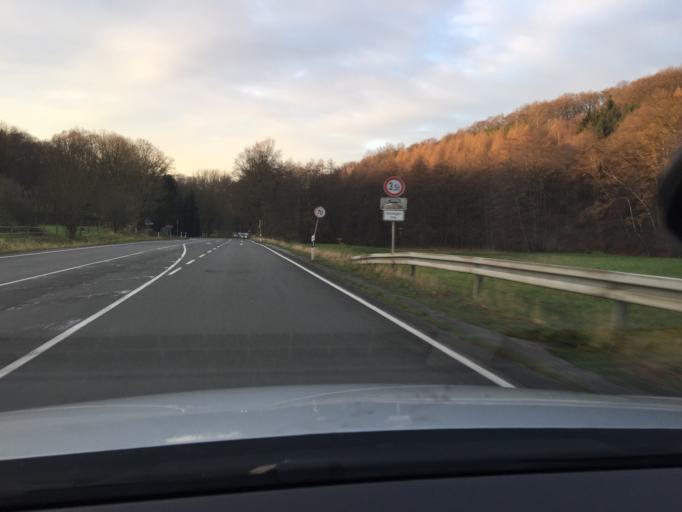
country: DE
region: North Rhine-Westphalia
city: Hattingen
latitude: 51.3614
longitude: 7.1970
